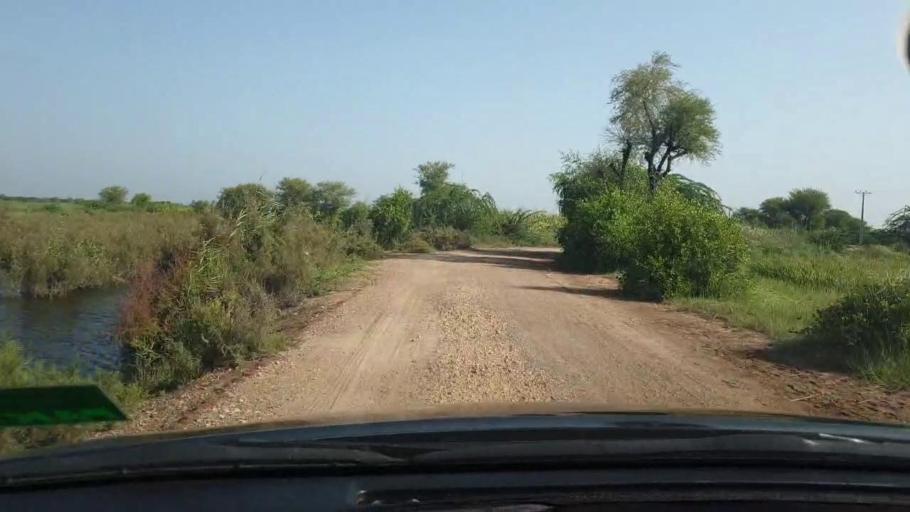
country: PK
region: Sindh
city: Tando Bago
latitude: 24.7133
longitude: 68.9886
